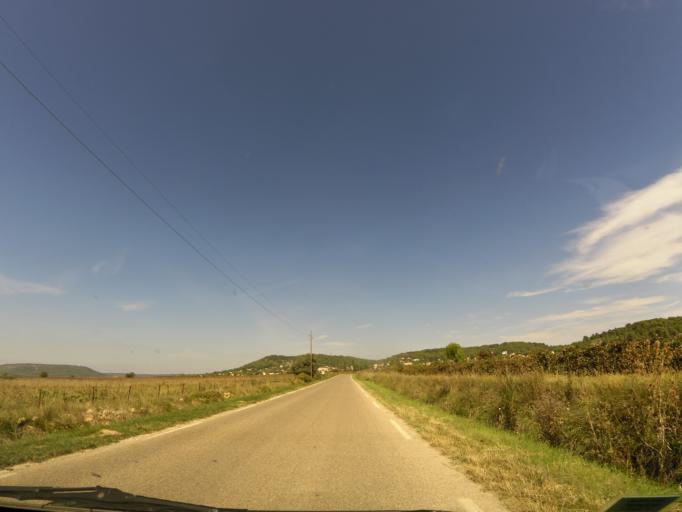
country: FR
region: Languedoc-Roussillon
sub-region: Departement du Gard
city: Nages-et-Solorgues
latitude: 43.7796
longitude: 4.2336
